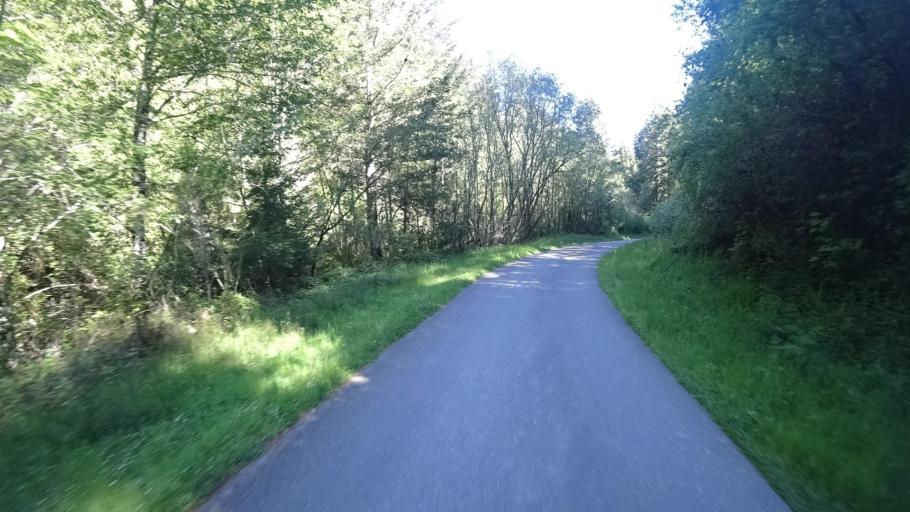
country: US
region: California
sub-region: Humboldt County
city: Ferndale
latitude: 40.5068
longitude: -124.2008
